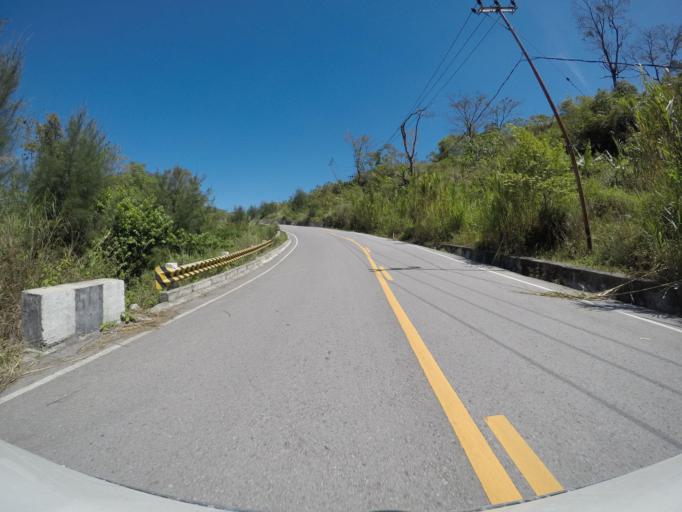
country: TL
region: Manatuto
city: Manatuto
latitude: -8.7765
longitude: 125.9653
